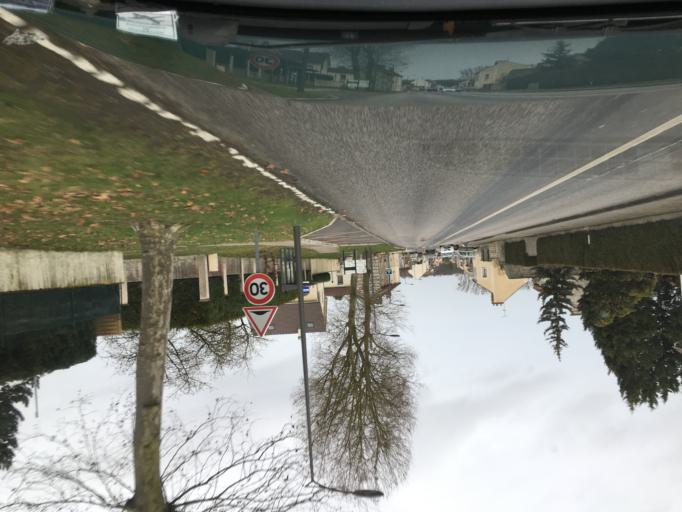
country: FR
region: Picardie
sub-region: Departement de l'Oise
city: Thiers-sur-Theve
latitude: 49.1505
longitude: 2.5467
